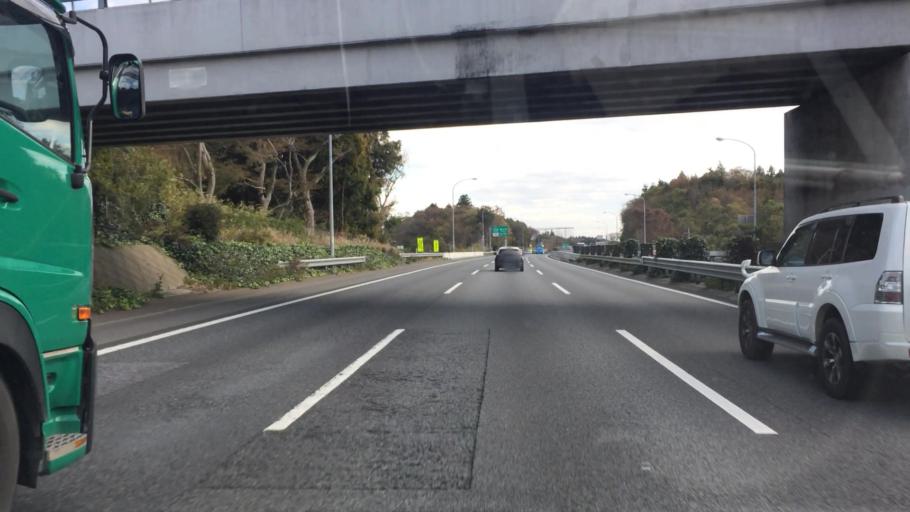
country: JP
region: Chiba
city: Sakura
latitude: 35.6854
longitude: 140.2229
